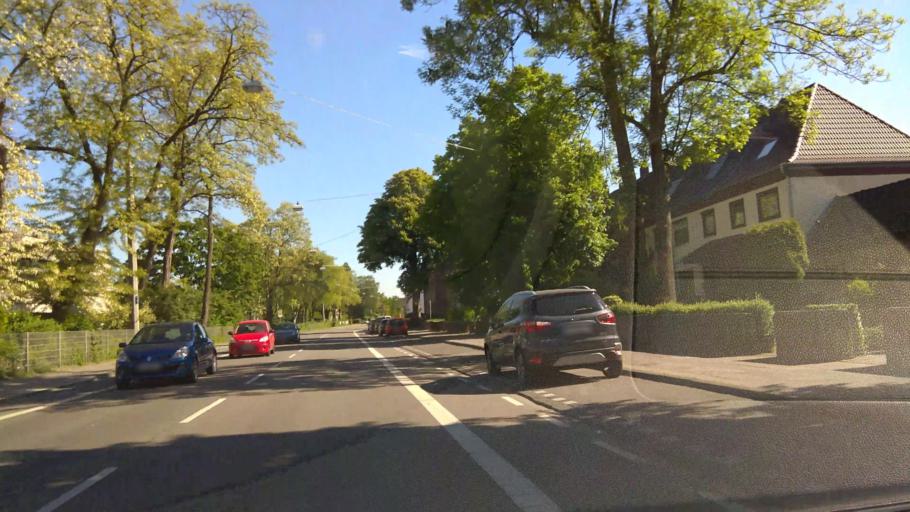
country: DE
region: North Rhine-Westphalia
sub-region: Regierungsbezirk Munster
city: Bottrop
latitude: 51.5269
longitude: 6.9370
